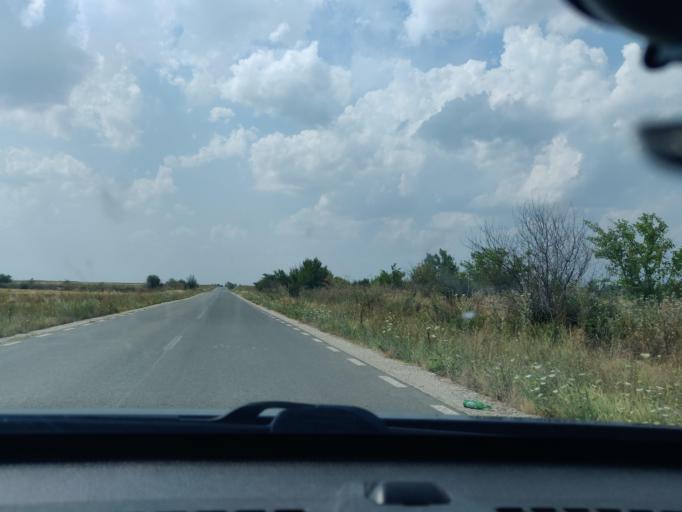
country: RO
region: Teleorman
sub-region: Comuna Gratia
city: Draghinesti
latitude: 44.4470
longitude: 25.4280
